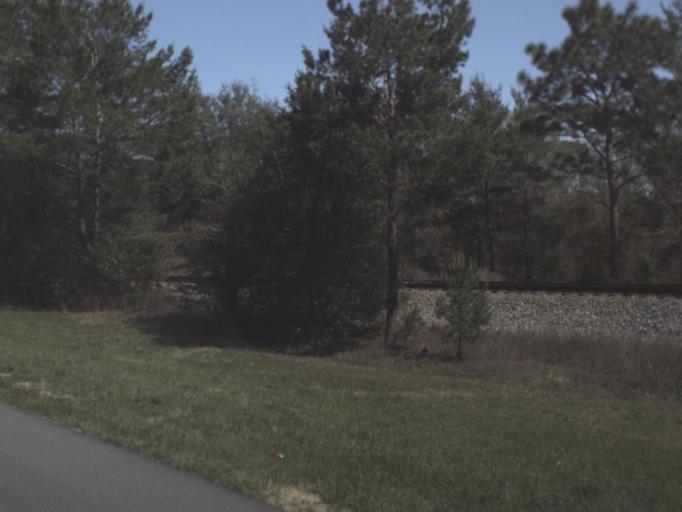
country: US
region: Florida
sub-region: Walton County
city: DeFuniak Springs
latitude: 30.7458
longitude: -86.3049
